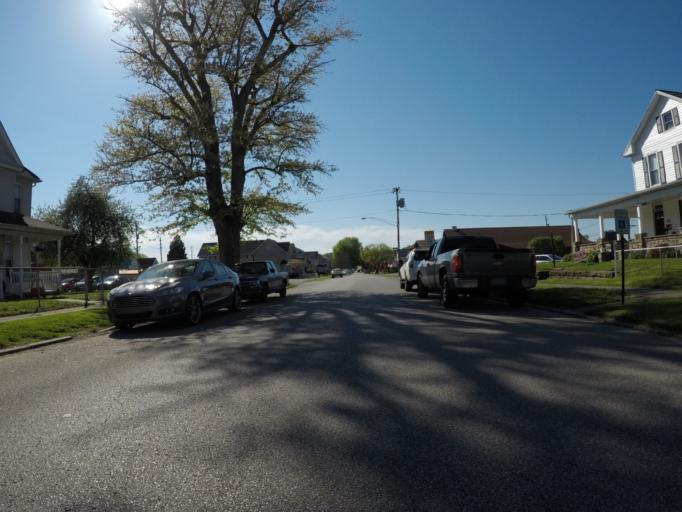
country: US
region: West Virginia
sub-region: Wayne County
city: Kenova
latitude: 38.4008
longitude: -82.5831
